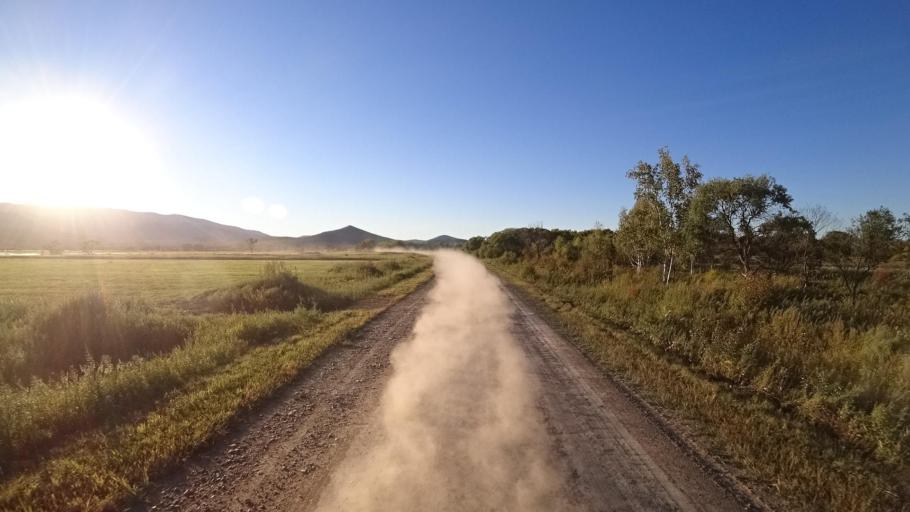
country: RU
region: Primorskiy
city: Kirovskiy
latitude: 44.8212
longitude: 133.6055
